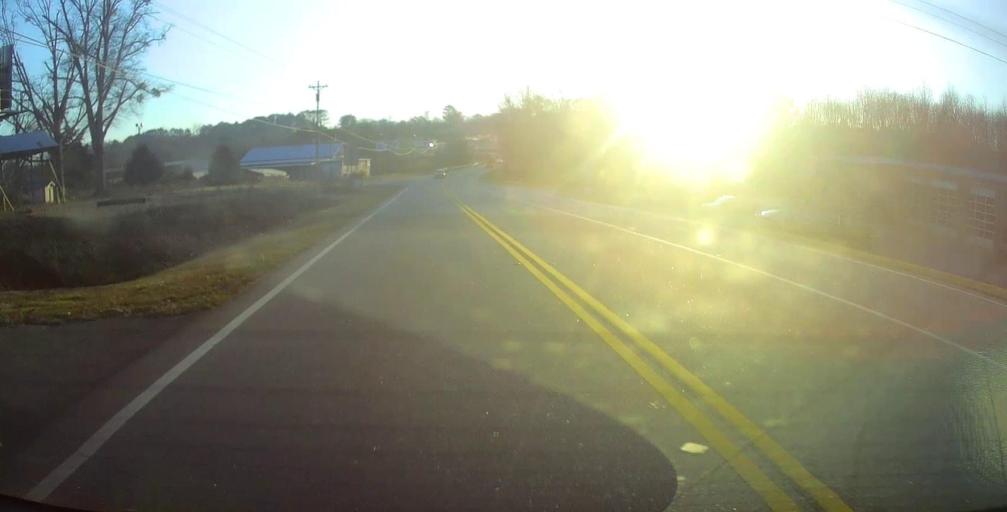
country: US
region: Georgia
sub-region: Troup County
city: La Grange
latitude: 33.0197
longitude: -85.0849
